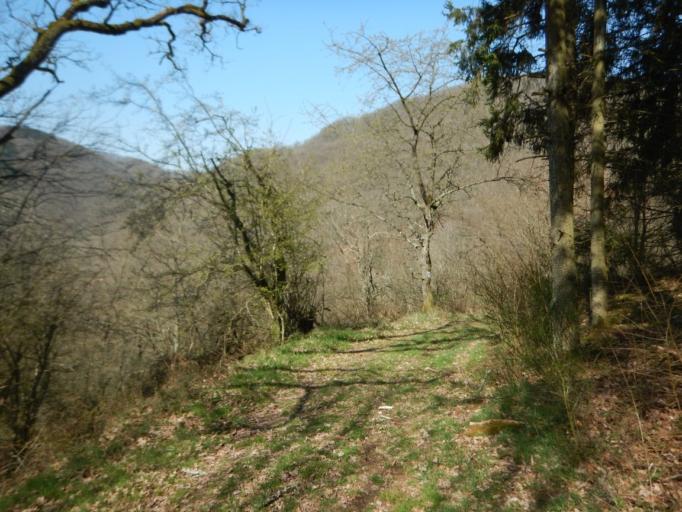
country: LU
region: Diekirch
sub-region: Canton de Diekirch
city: Bourscheid
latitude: 49.9343
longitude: 6.0730
